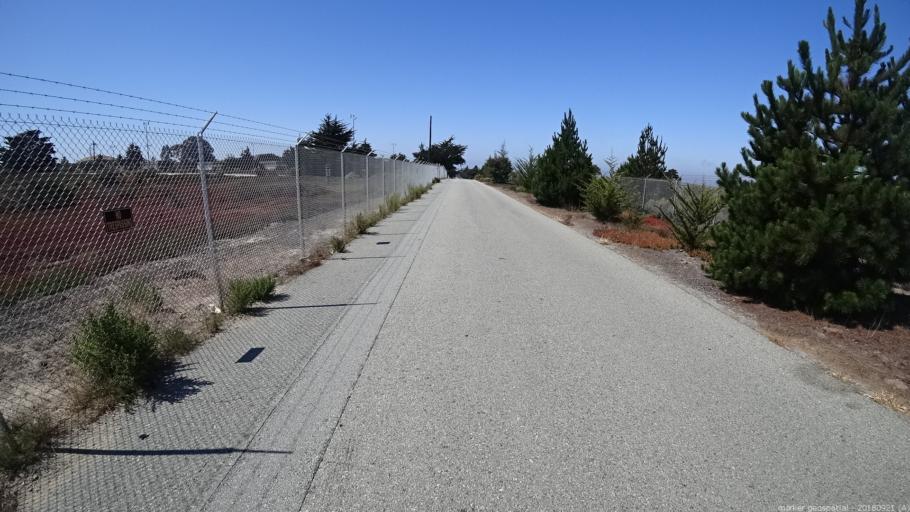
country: US
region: California
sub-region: Monterey County
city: Marina
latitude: 36.6463
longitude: -121.7877
